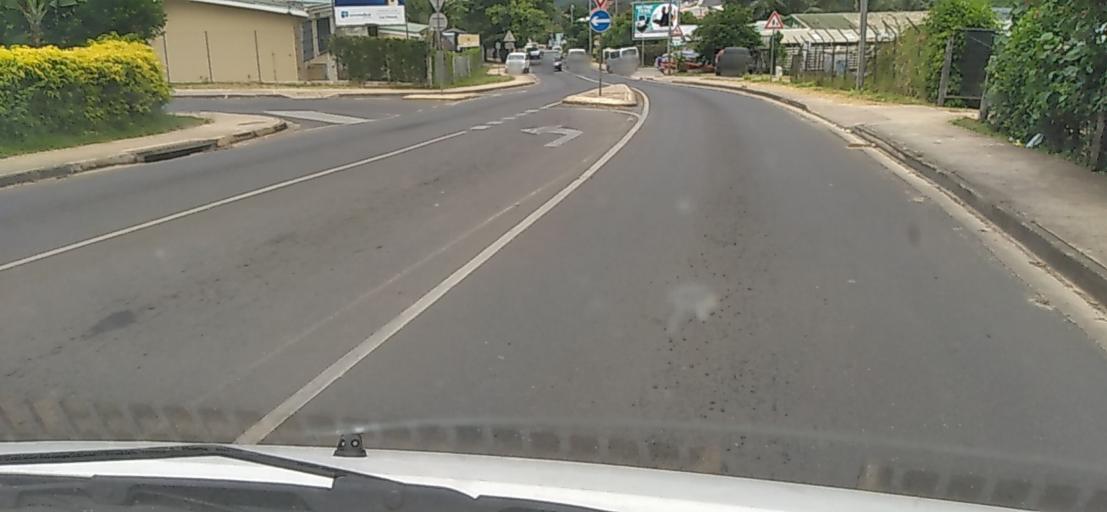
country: VU
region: Shefa
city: Port-Vila
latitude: -17.7379
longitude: 168.3203
